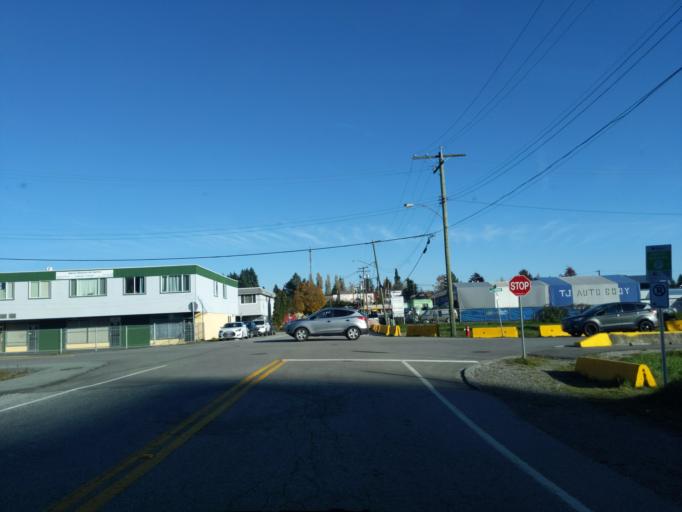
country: CA
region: British Columbia
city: New Westminster
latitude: 49.1931
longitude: -122.8486
